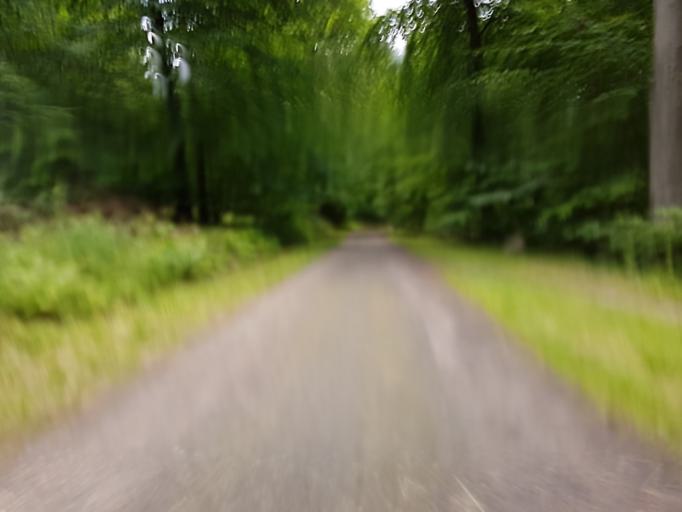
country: DK
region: Capital Region
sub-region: Fureso Kommune
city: Vaerlose
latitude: 55.7908
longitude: 12.3539
